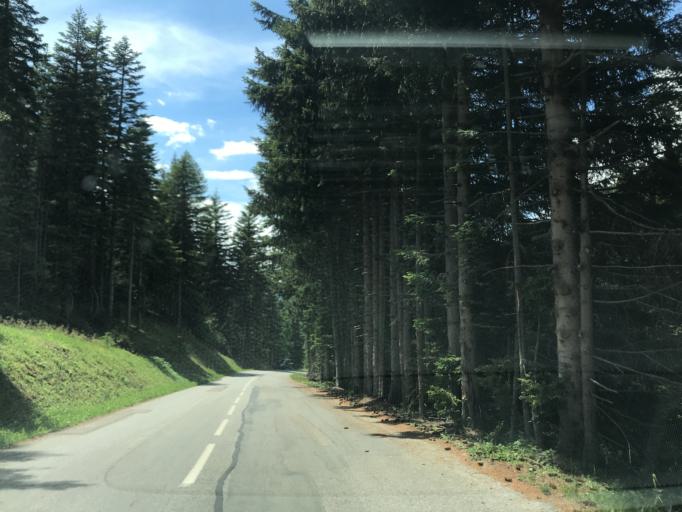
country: FR
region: Rhone-Alpes
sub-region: Departement de la Savoie
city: Modane
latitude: 45.2106
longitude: 6.6435
